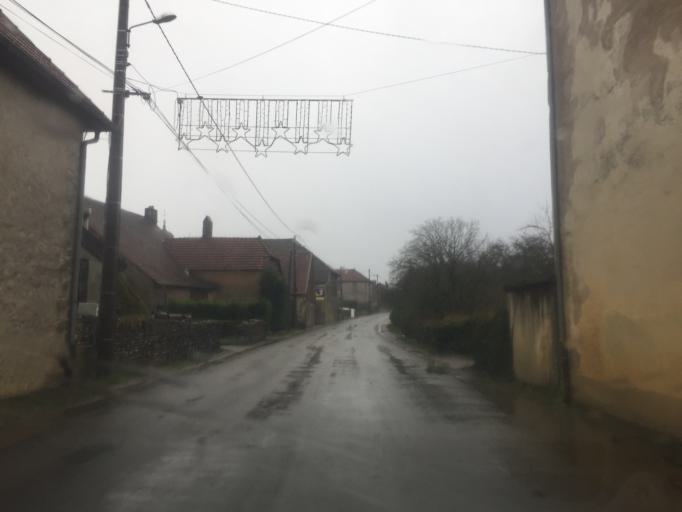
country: FR
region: Franche-Comte
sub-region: Departement du Jura
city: Dampierre
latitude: 47.2183
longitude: 5.7359
